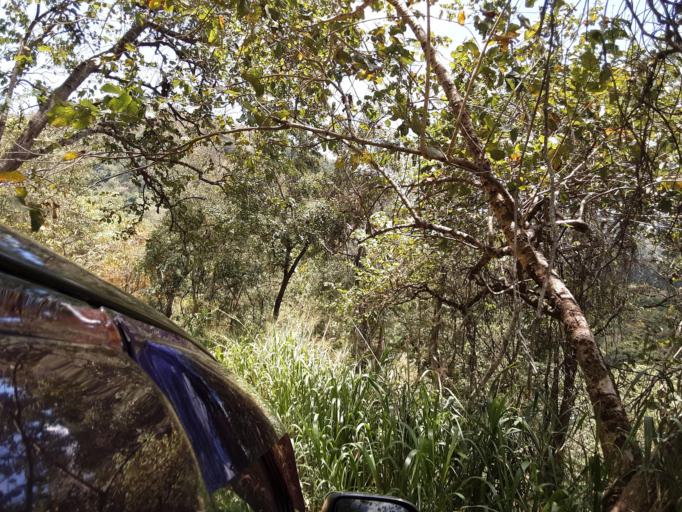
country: LK
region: Uva
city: Haputale
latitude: 6.8129
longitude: 81.1090
